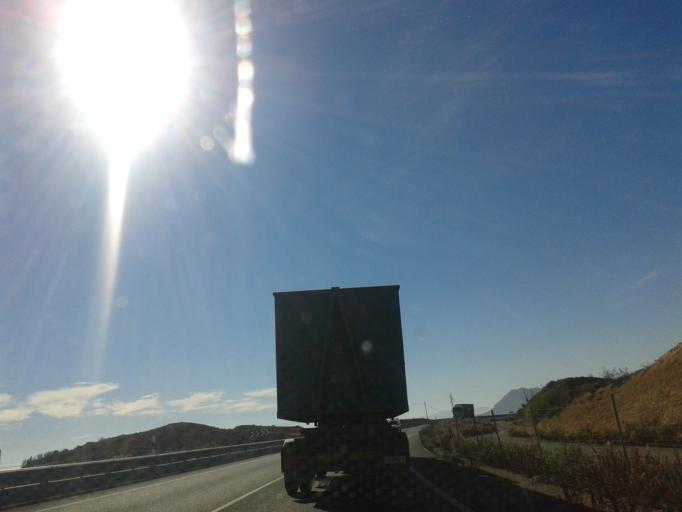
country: ES
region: Castille-La Mancha
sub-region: Provincia de Albacete
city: Caudete
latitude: 38.7277
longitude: -0.9424
